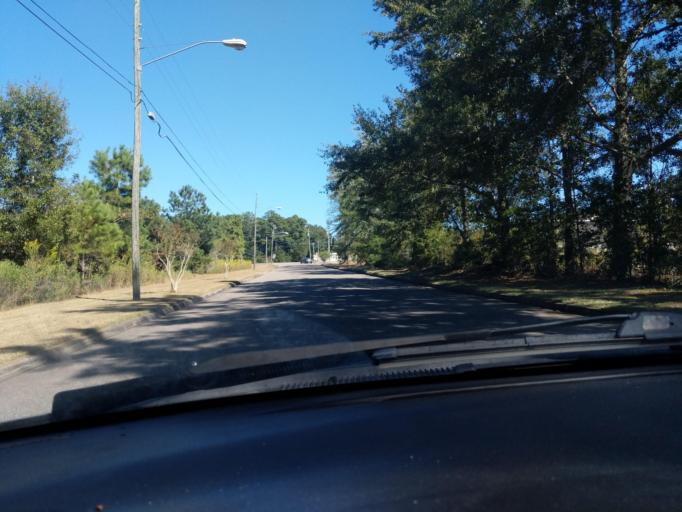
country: US
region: Alabama
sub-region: Houston County
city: Dothan
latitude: 31.1701
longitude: -85.4041
